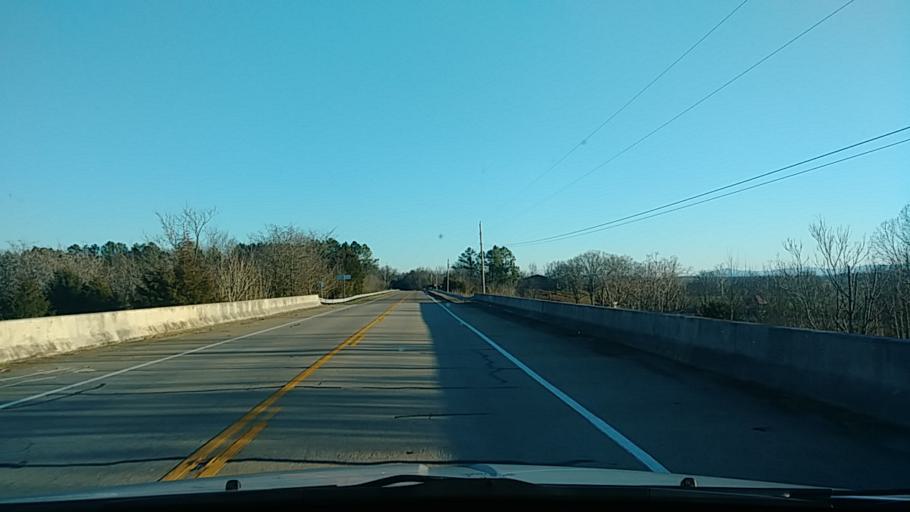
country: US
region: Tennessee
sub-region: Hamblen County
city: Morristown
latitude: 36.1856
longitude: -83.1682
